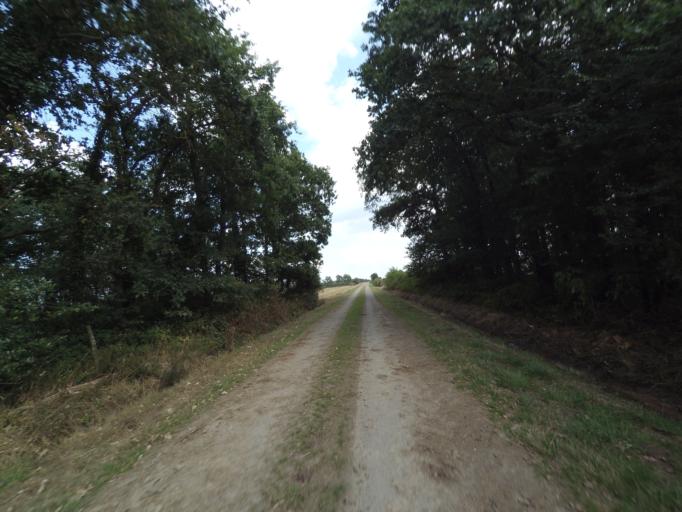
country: FR
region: Pays de la Loire
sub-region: Departement de la Vendee
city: Saint-Andre-Treize-Voies
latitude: 46.9691
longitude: -1.3923
